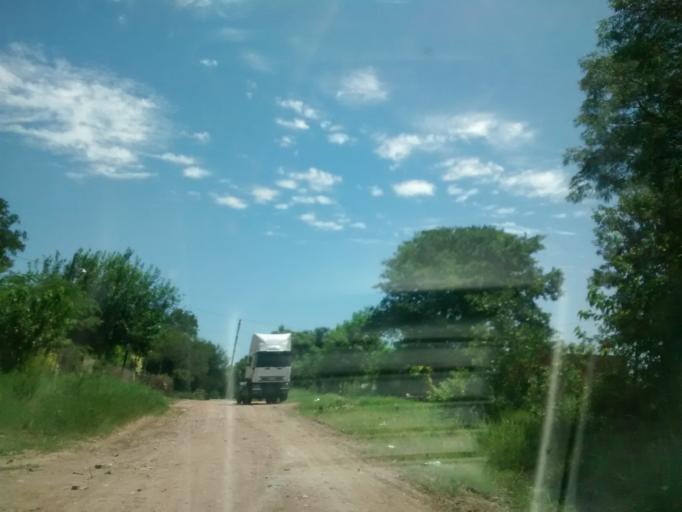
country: AR
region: Chaco
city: Resistencia
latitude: -27.4242
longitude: -58.9714
